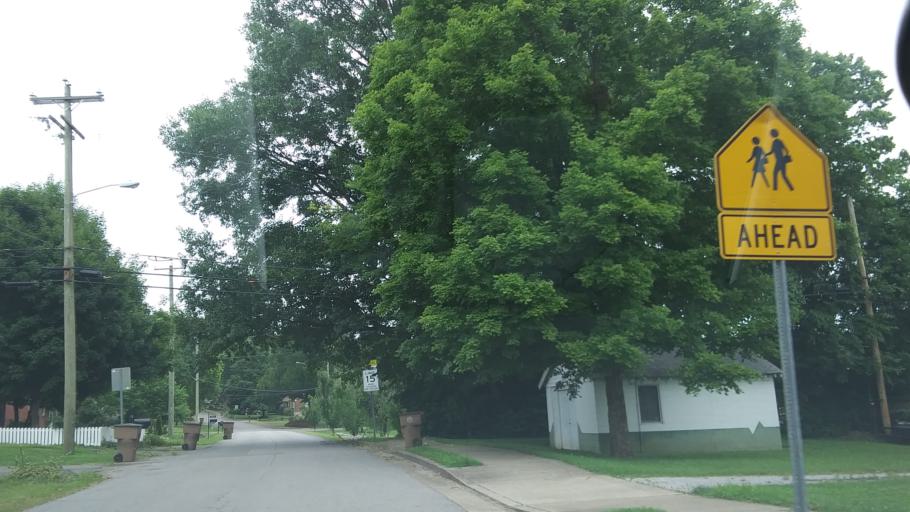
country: US
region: Tennessee
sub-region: Davidson County
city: Belle Meade
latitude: 36.1413
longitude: -86.8543
